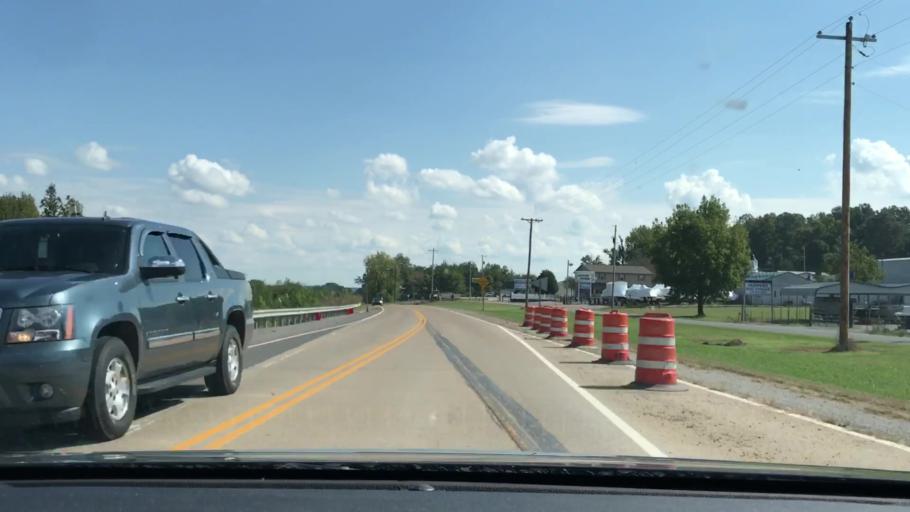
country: US
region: Kentucky
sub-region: Trigg County
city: Cadiz
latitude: 36.7983
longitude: -87.9656
